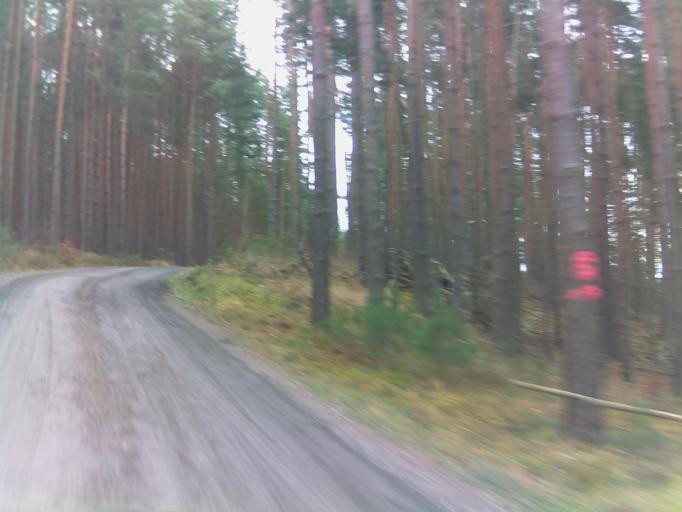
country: DE
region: Thuringia
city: Orlamunde
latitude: 50.7498
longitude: 11.4657
